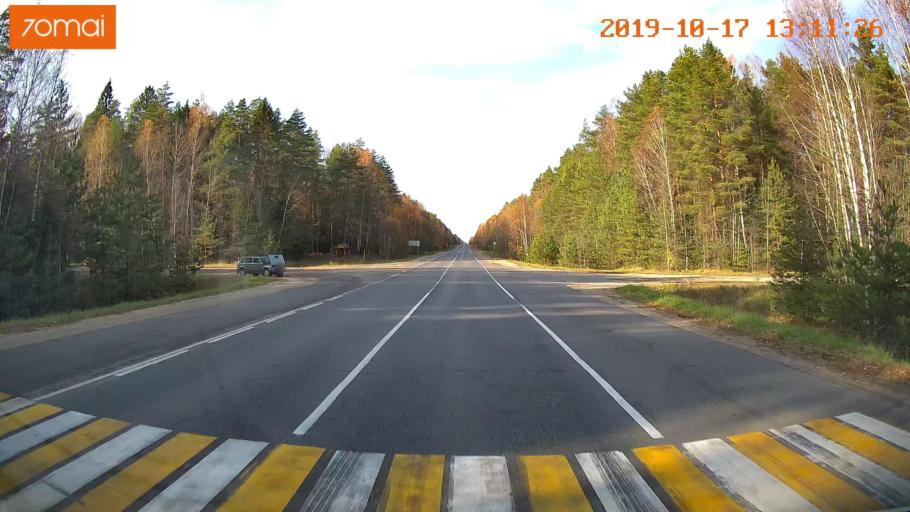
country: RU
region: Rjazan
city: Syntul
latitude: 55.0275
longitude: 41.2355
